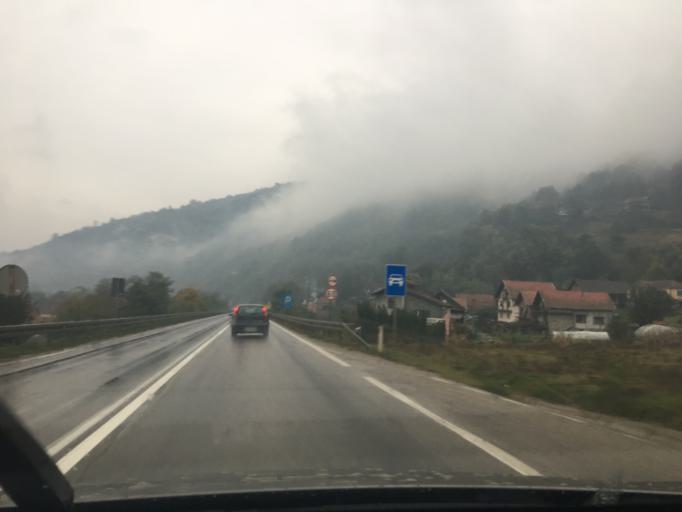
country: RS
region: Central Serbia
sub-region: Pcinjski Okrug
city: Vladicin Han
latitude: 42.7748
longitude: 22.0921
